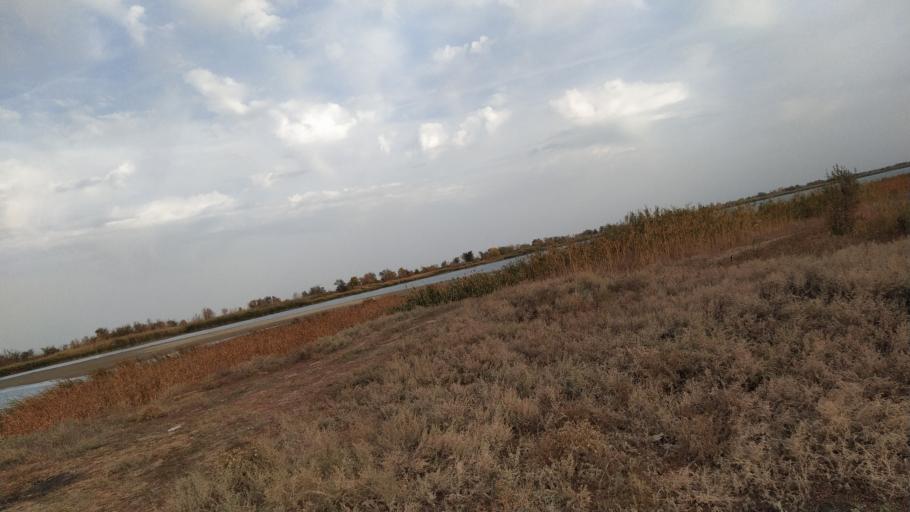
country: RU
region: Rostov
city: Kuleshovka
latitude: 47.1414
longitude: 39.5812
